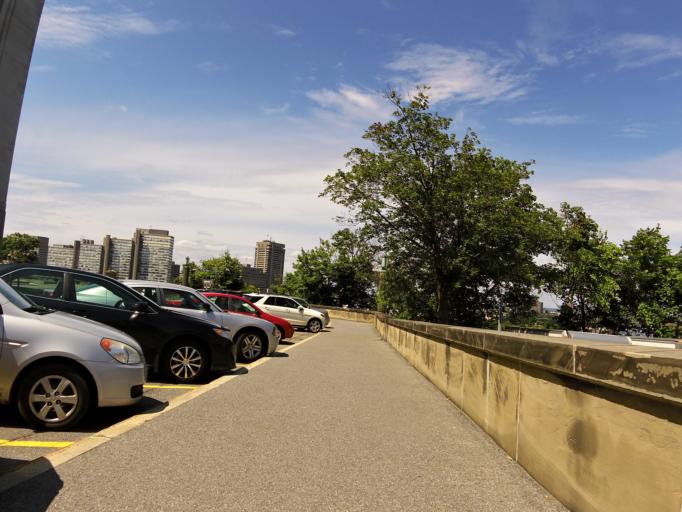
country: CA
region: Ontario
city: Ottawa
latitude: 45.4222
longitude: -75.7050
